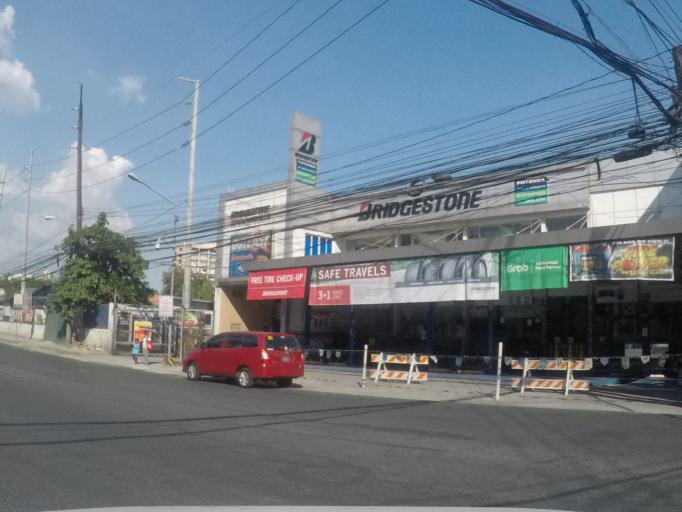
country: PH
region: Metro Manila
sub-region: San Juan
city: San Juan
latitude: 14.6059
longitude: 121.0370
